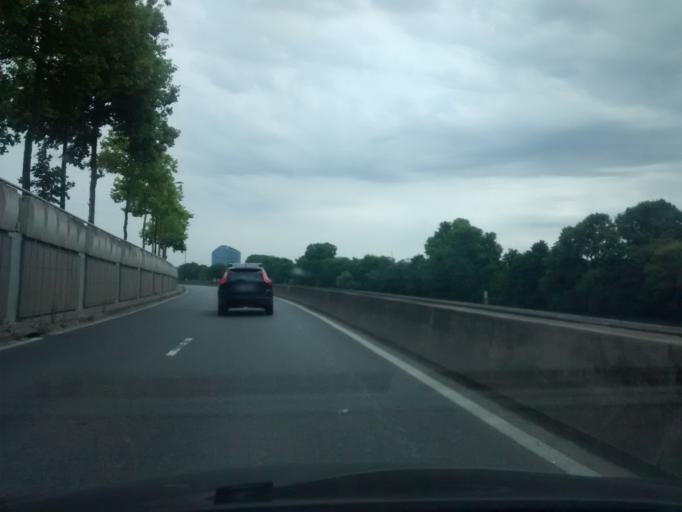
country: FR
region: Ile-de-France
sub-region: Departement des Hauts-de-Seine
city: Boulogne-Billancourt
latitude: 48.8252
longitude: 2.2492
